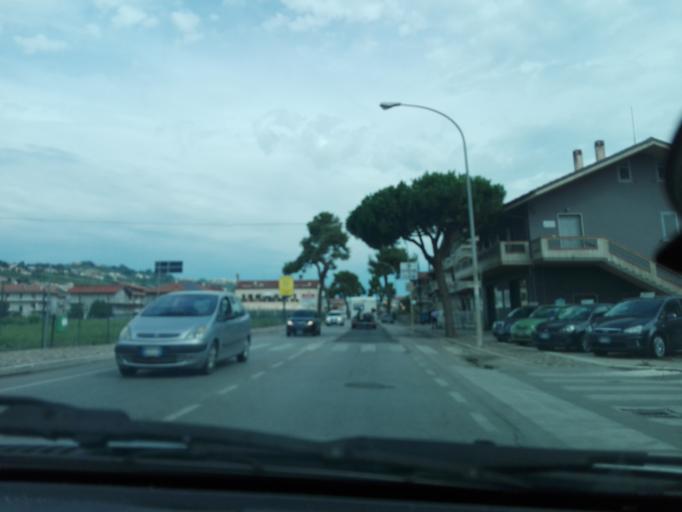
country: IT
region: Abruzzo
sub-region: Provincia di Teramo
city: Silvi
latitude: 42.5426
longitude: 14.1230
